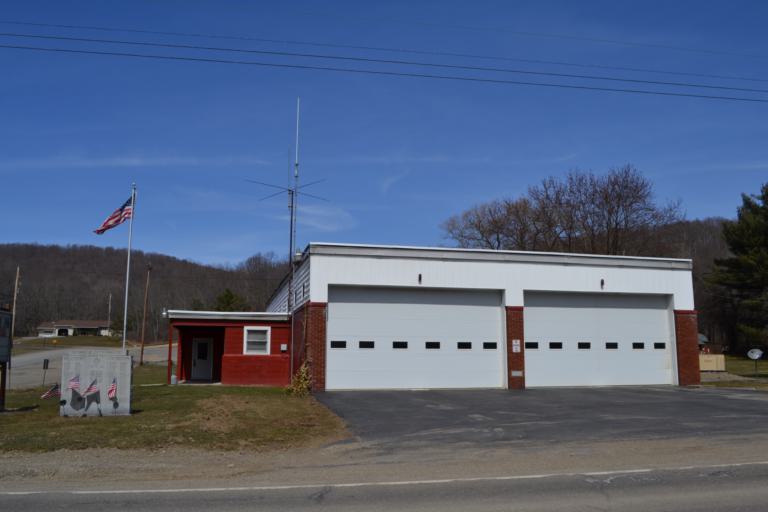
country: US
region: Pennsylvania
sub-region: McKean County
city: Foster Brook
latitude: 41.9718
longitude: -78.5753
